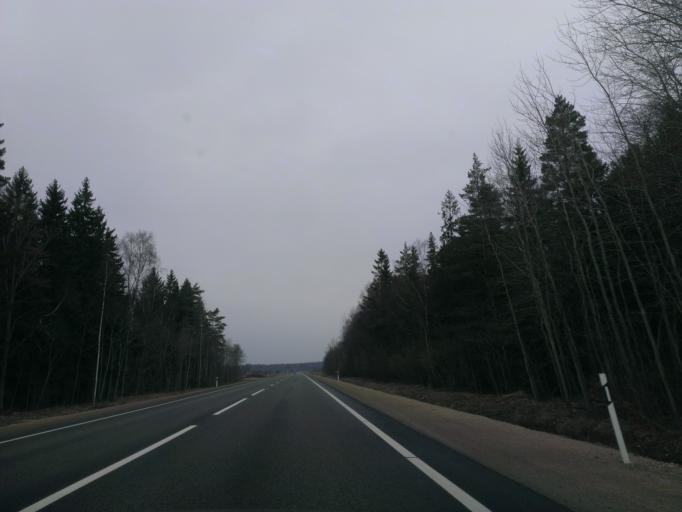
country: LV
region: Salacgrivas
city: Salacgriva
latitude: 57.7127
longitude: 24.3660
